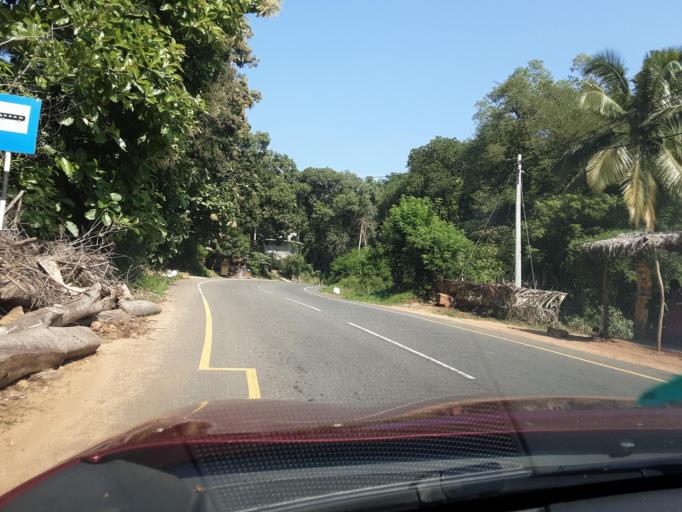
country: LK
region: Uva
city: Badulla
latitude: 7.1605
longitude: 81.0517
